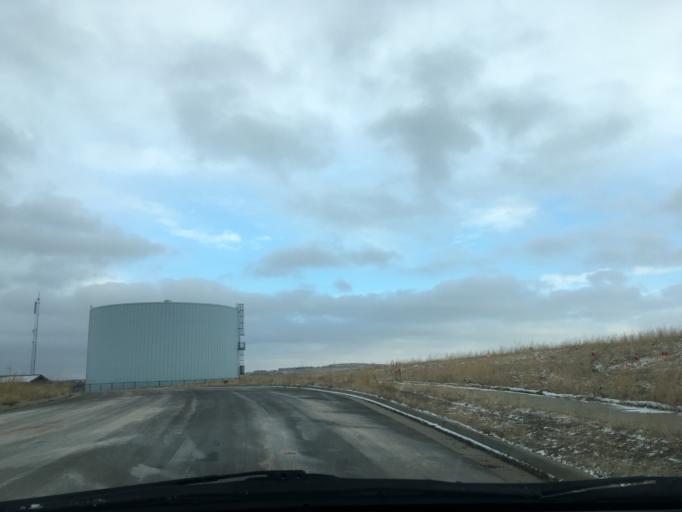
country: US
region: Colorado
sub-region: Boulder County
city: Lafayette
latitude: 39.9777
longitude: -105.0644
